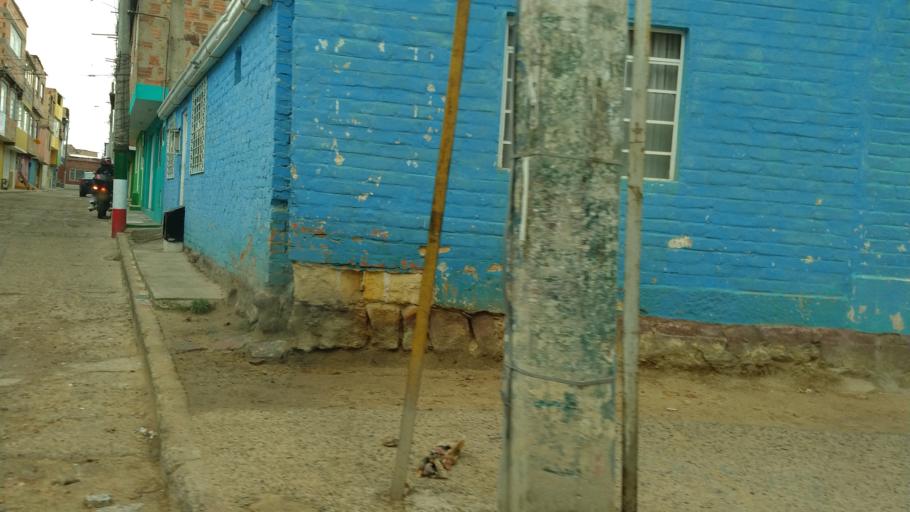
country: CO
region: Cundinamarca
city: Soacha
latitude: 4.5737
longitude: -74.2229
